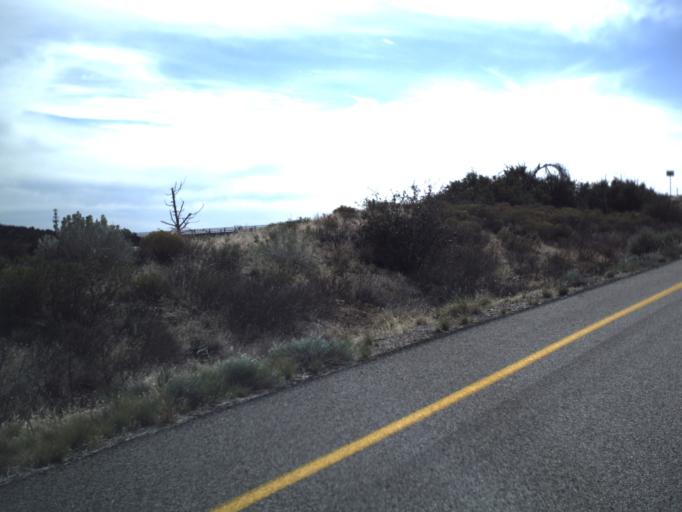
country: US
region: Utah
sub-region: Washington County
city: Toquerville
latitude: 37.3283
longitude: -113.2845
